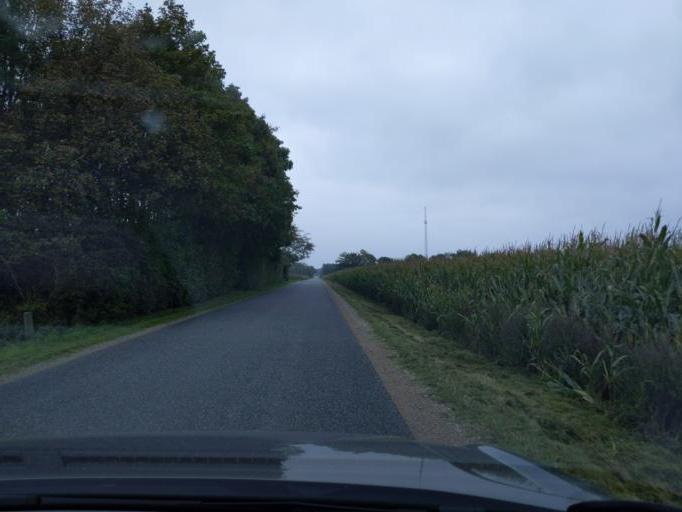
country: DK
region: Central Jutland
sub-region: Viborg Kommune
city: Karup
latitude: 56.3676
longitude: 9.2358
